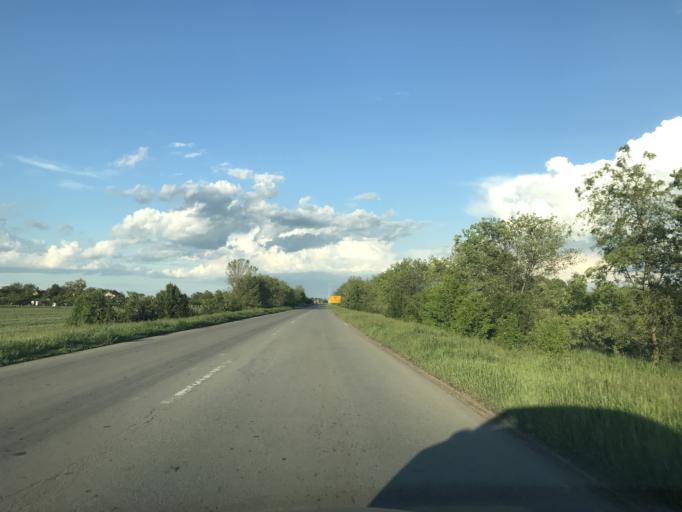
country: RS
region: Autonomna Pokrajina Vojvodina
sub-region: Srednjebanatski Okrug
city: Zrenjanin
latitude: 45.4012
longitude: 20.3710
